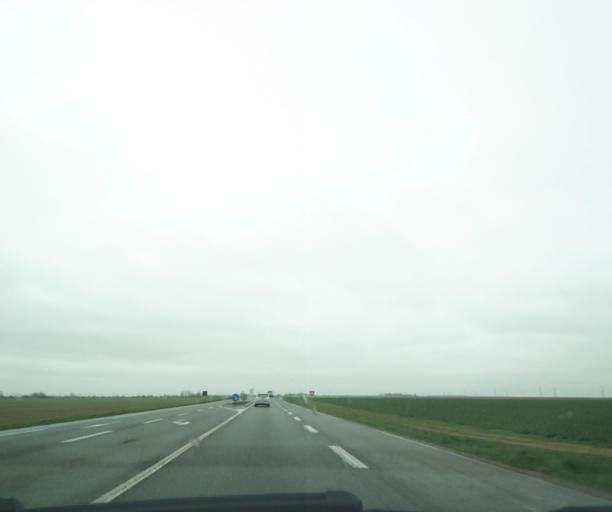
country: FR
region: Ile-de-France
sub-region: Departement de l'Essonne
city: Angerville
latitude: 48.2787
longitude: 1.9775
